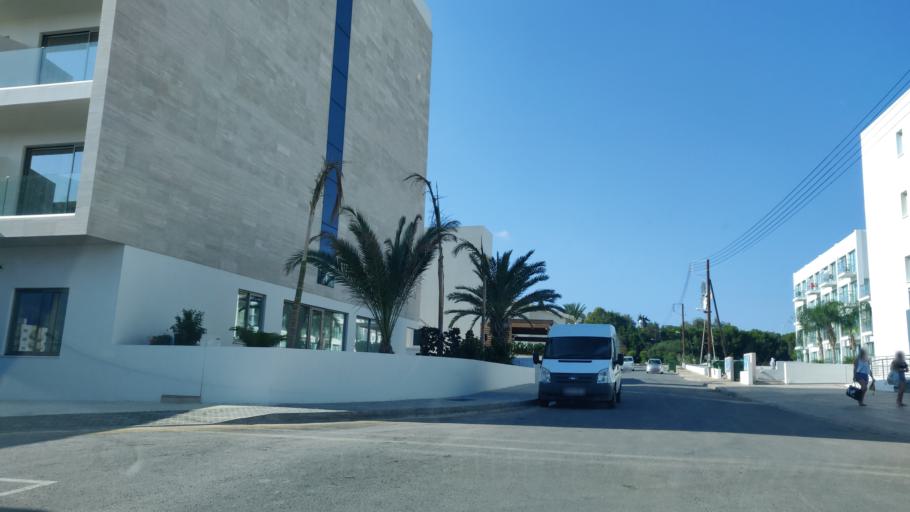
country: CY
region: Ammochostos
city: Protaras
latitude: 35.0074
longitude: 34.0607
